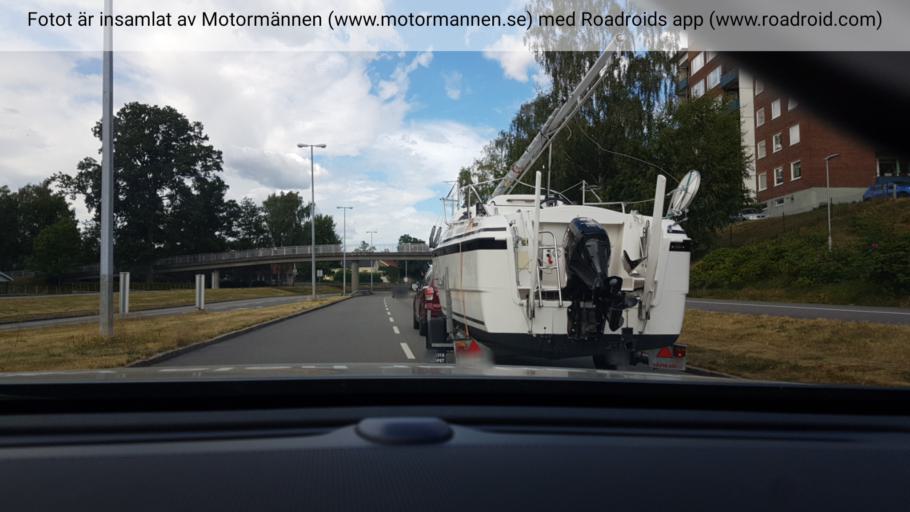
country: SE
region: Skane
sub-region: Hassleholms Kommun
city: Hassleholm
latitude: 56.1582
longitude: 13.7554
